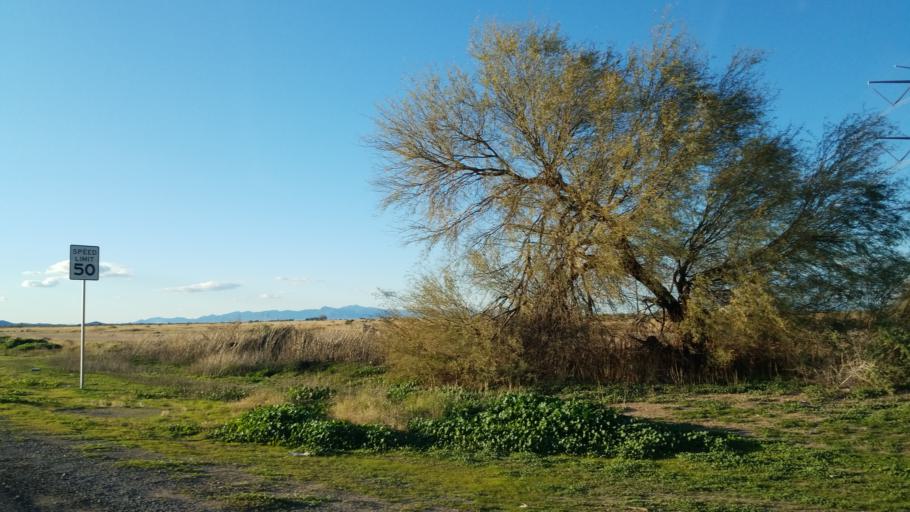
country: US
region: Arizona
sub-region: Maricopa County
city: Laveen
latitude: 33.3485
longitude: -112.1940
